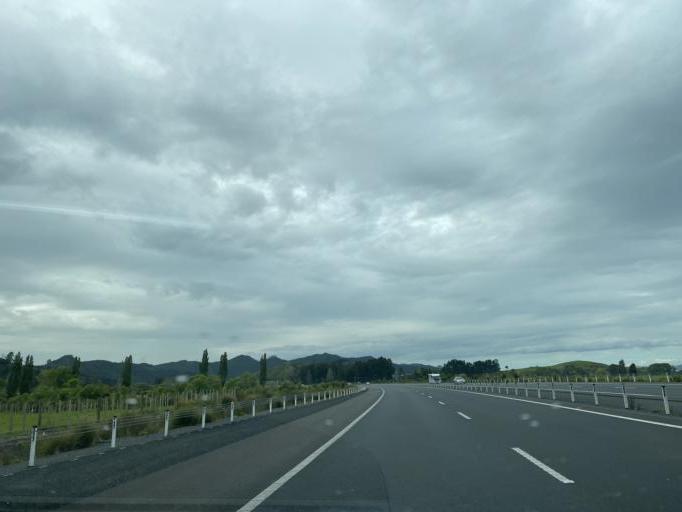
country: NZ
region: Waikato
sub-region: Waikato District
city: Ngaruawahia
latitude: -37.6038
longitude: 175.2057
